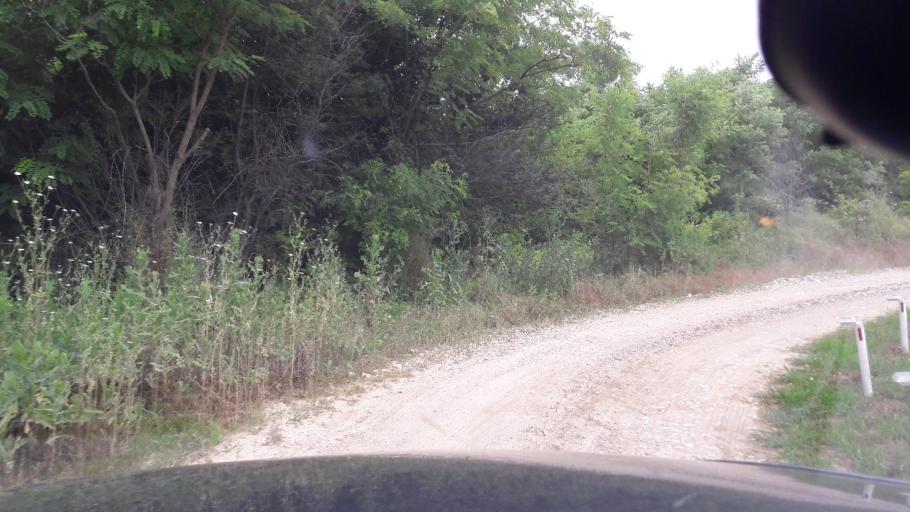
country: RS
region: Central Serbia
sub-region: Belgrade
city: Sopot
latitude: 44.6015
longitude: 20.5988
